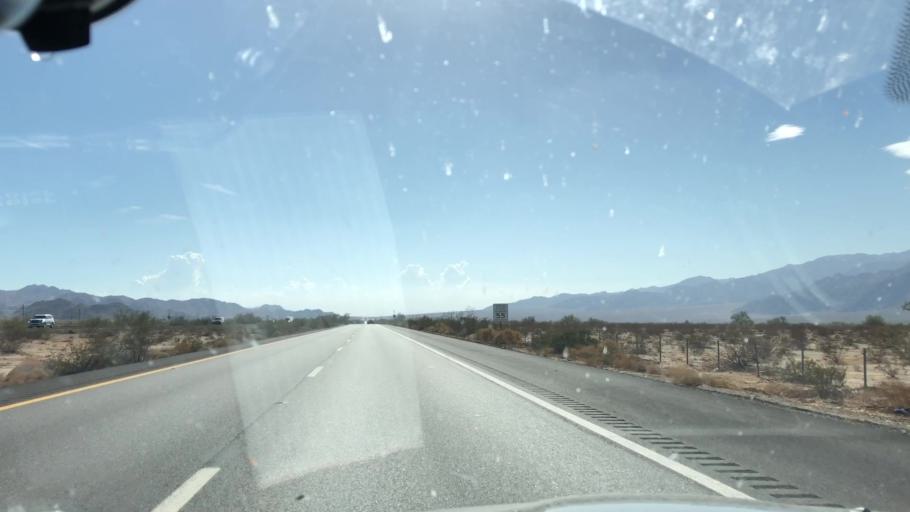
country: US
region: California
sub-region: Imperial County
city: Niland
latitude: 33.6732
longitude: -115.5889
